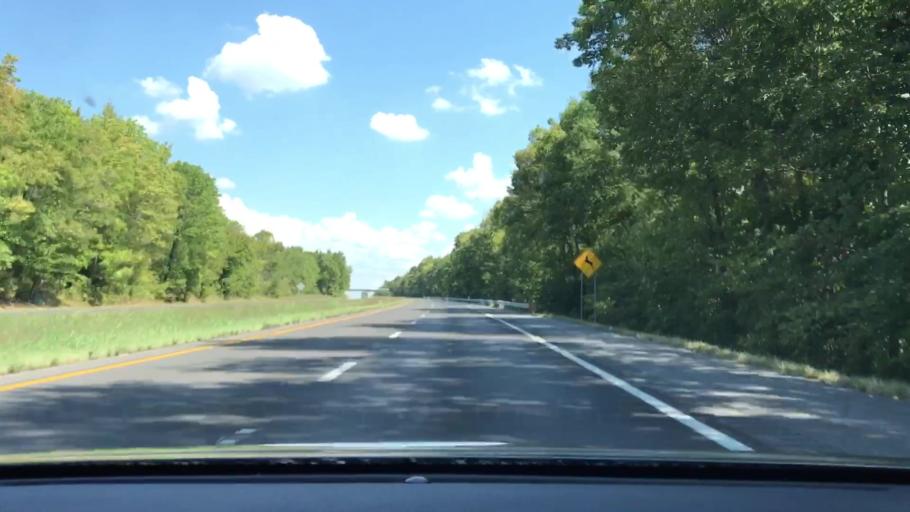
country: US
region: Kentucky
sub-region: Fulton County
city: Fulton
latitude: 36.6019
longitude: -88.7986
